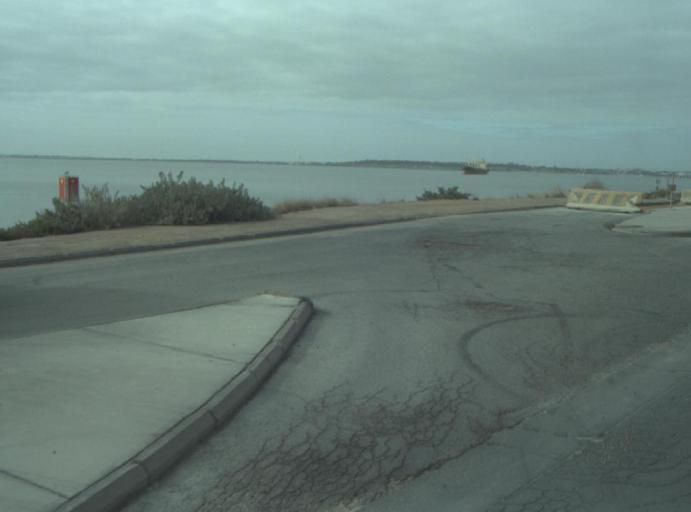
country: AU
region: Victoria
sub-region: Greater Geelong
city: Bell Park
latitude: -38.0972
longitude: 144.3799
